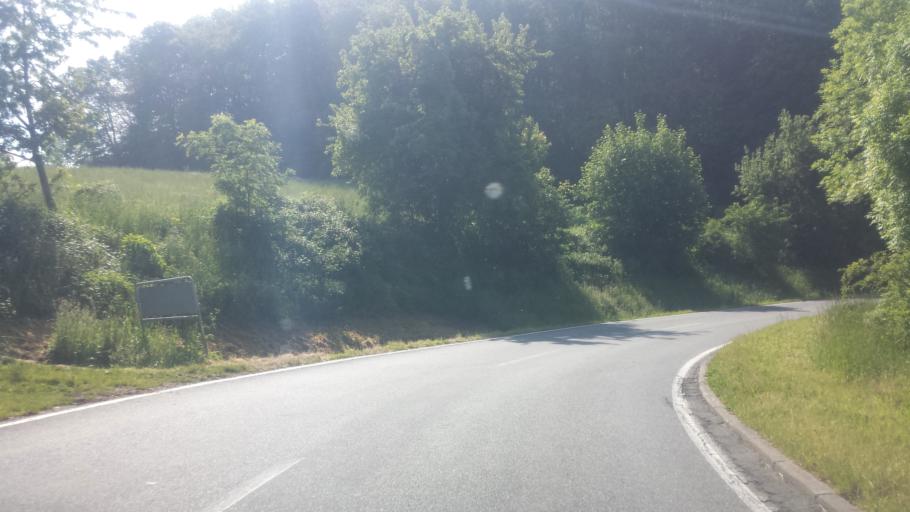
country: DE
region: Hesse
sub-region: Regierungsbezirk Darmstadt
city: Rimbach
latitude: 49.5894
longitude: 8.7771
